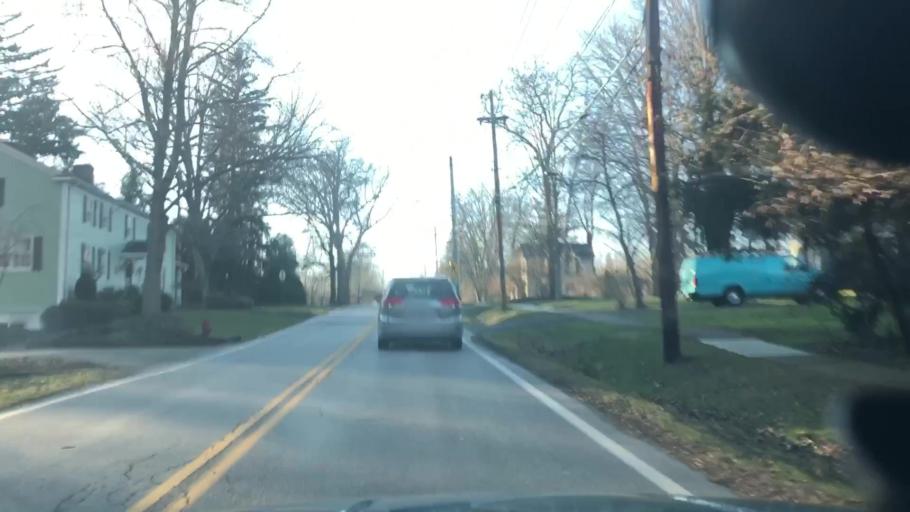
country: US
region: Ohio
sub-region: Cuyahoga County
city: Olmsted Falls
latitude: 41.3787
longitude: -81.9000
